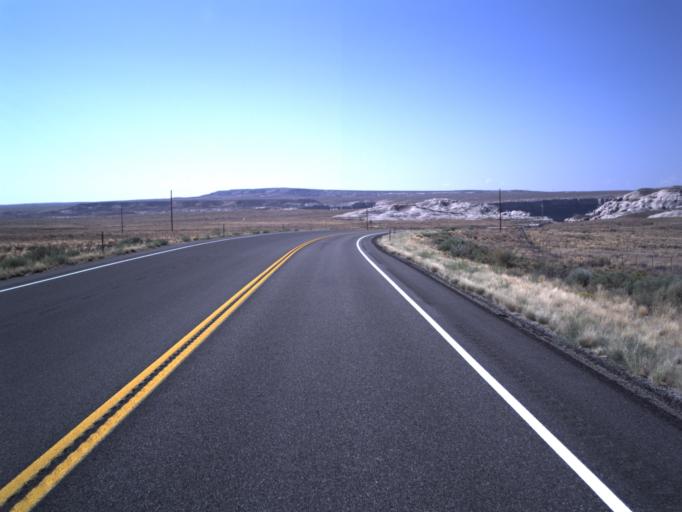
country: US
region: Utah
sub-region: San Juan County
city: Blanding
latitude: 37.3074
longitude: -109.5283
